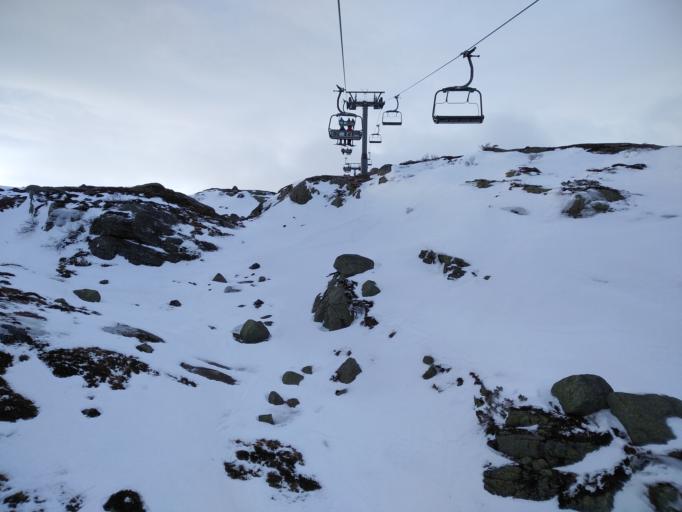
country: NO
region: Vest-Agder
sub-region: Sirdal
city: Tonstad
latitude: 58.9126
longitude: 6.8238
